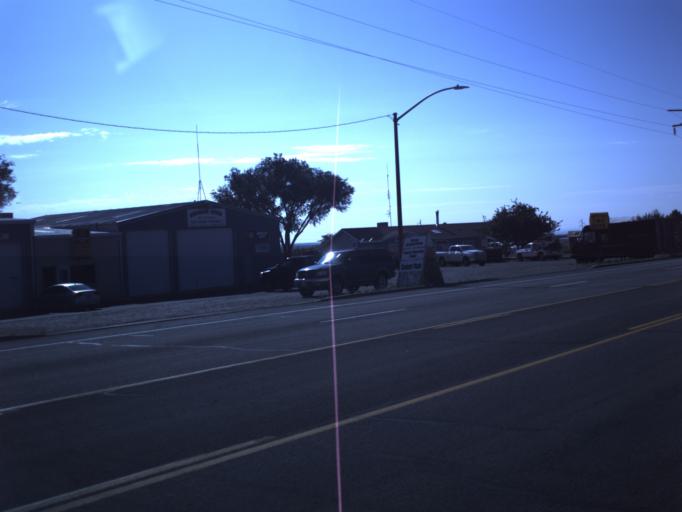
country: US
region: Utah
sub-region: San Juan County
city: Blanding
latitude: 37.5982
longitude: -109.4787
